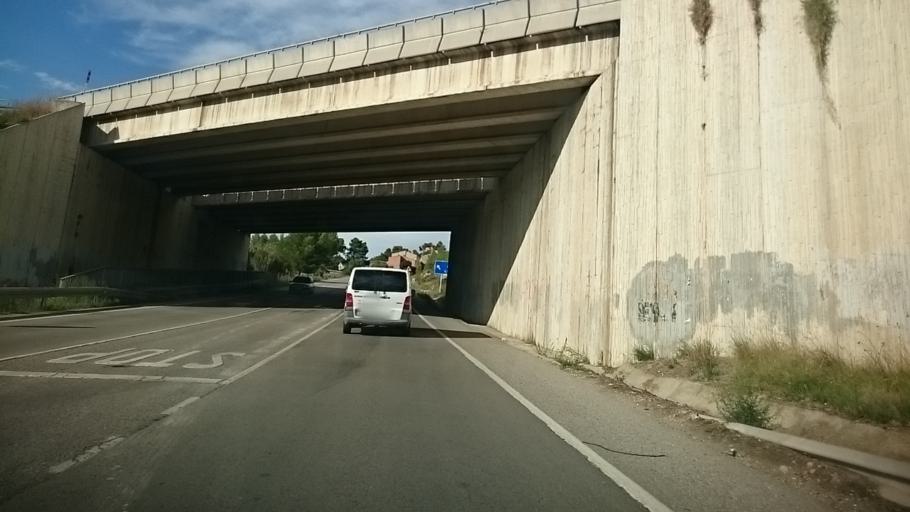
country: ES
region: Catalonia
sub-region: Provincia de Barcelona
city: Odena
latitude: 41.5997
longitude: 1.6356
